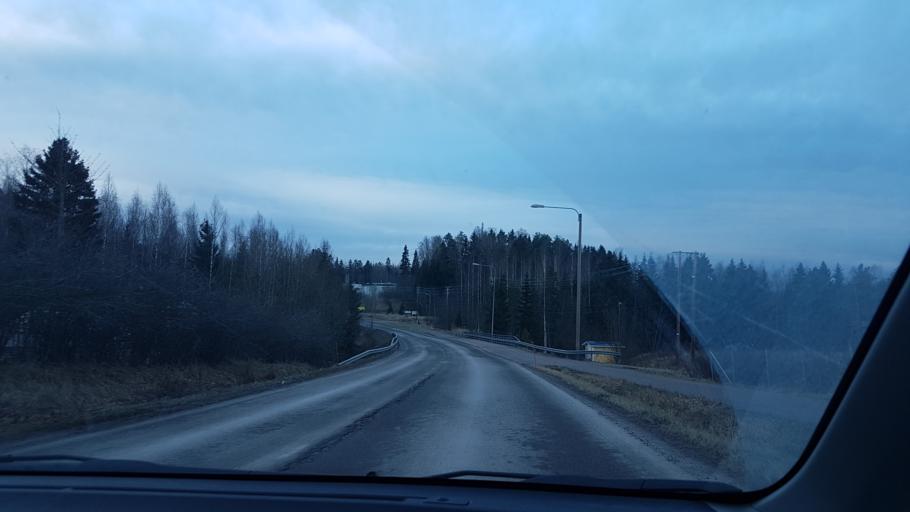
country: FI
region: Uusimaa
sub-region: Helsinki
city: Nurmijaervi
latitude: 60.3621
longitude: 24.7454
